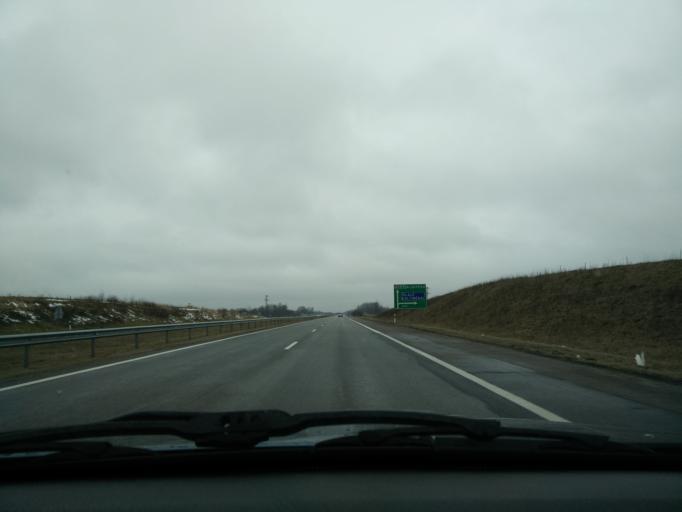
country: LT
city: Silale
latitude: 55.5345
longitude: 22.3232
